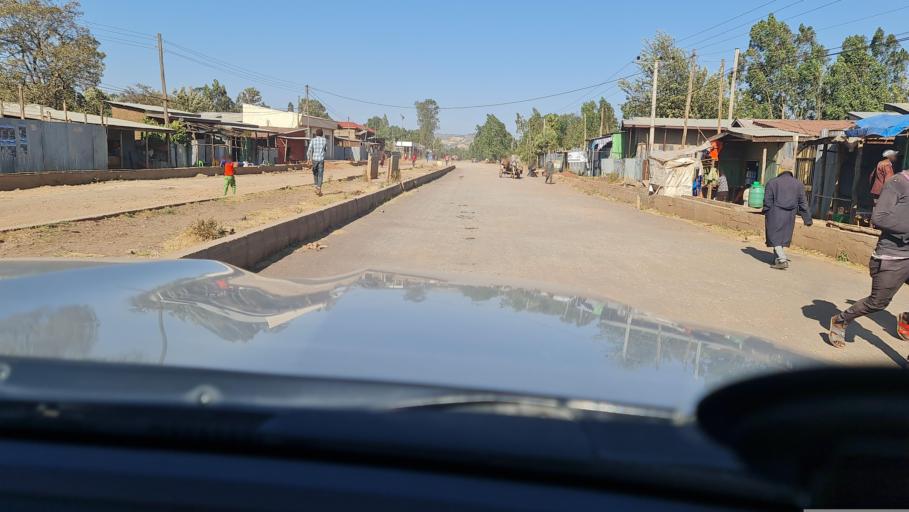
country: ET
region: Oromiya
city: Waliso
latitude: 8.5456
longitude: 37.9634
